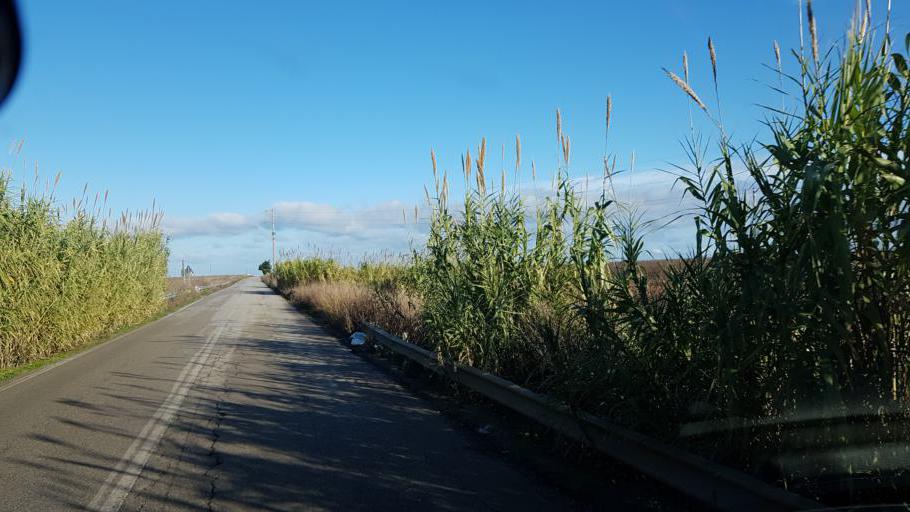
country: IT
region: Apulia
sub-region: Provincia di Brindisi
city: Tuturano
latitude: 40.5692
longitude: 17.9493
